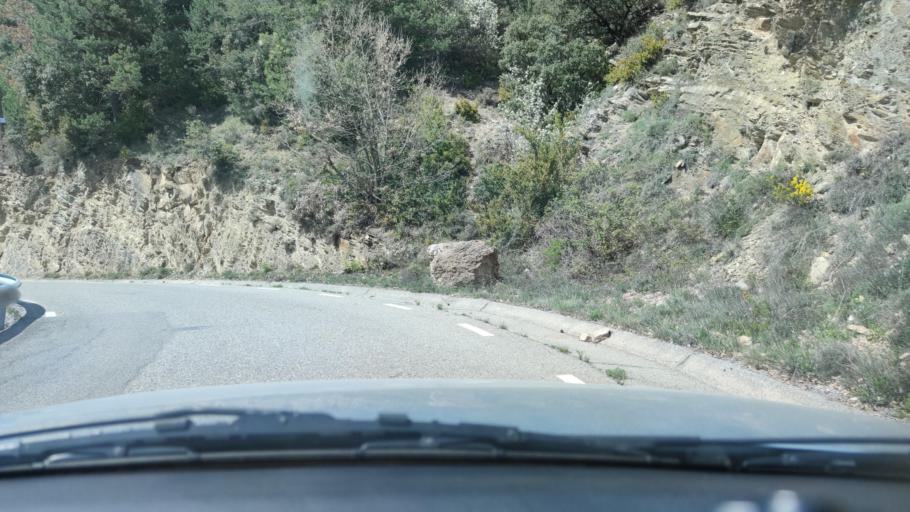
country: ES
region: Catalonia
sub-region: Provincia de Lleida
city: Coll de Nargo
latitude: 42.2956
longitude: 1.2694
